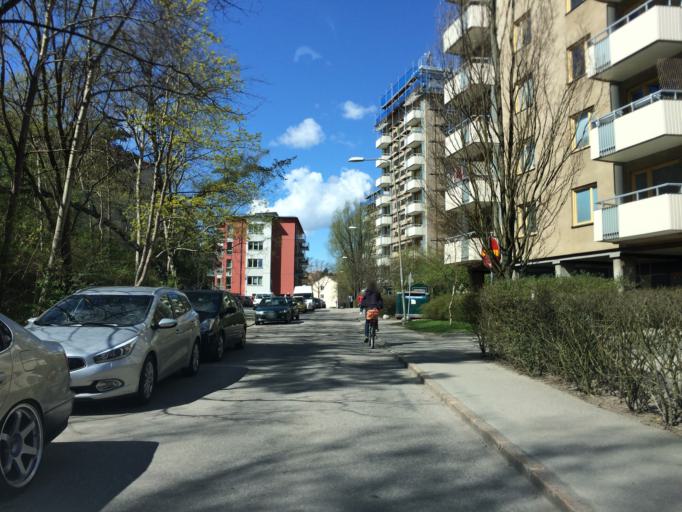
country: SE
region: Stockholm
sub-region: Huddinge Kommun
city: Segeltorp
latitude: 59.2945
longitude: 17.9754
